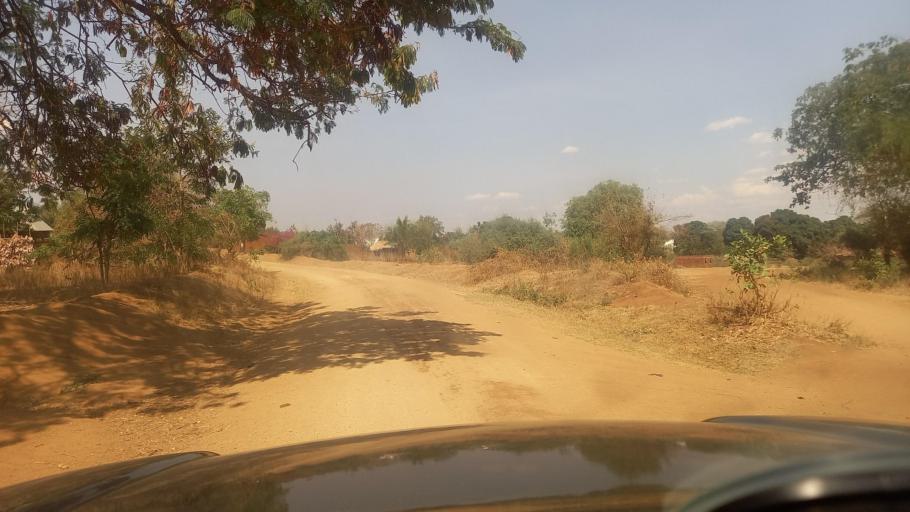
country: TZ
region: Morogoro
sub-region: Kilosa
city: Magole
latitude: -6.3211
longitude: 37.3750
